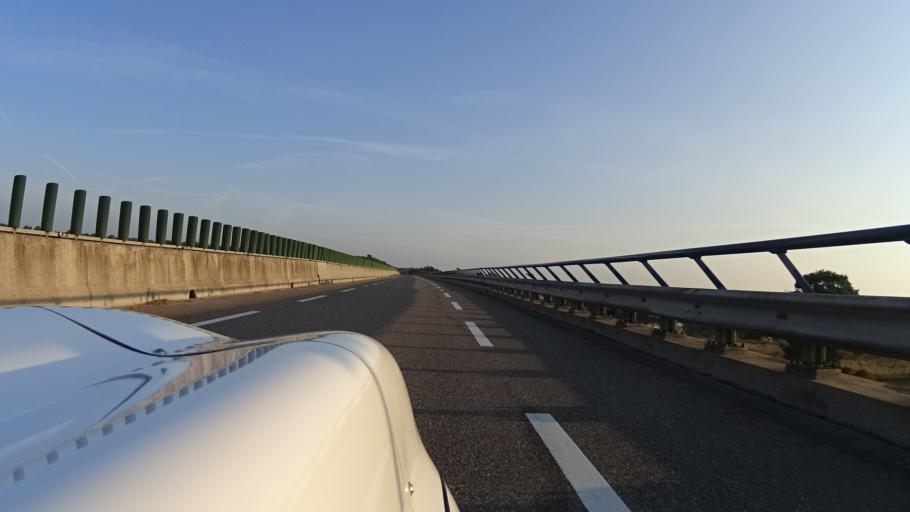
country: NL
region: Limburg
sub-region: Gemeente Bergen
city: Wellerlooi
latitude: 51.5459
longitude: 6.1000
